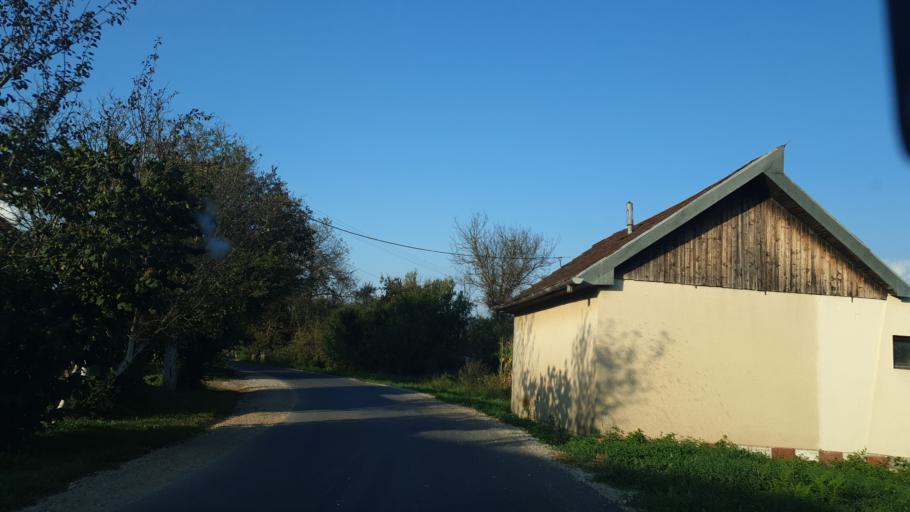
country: RS
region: Central Serbia
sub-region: Zlatiborski Okrug
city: Pozega
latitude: 43.8587
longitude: 19.9832
